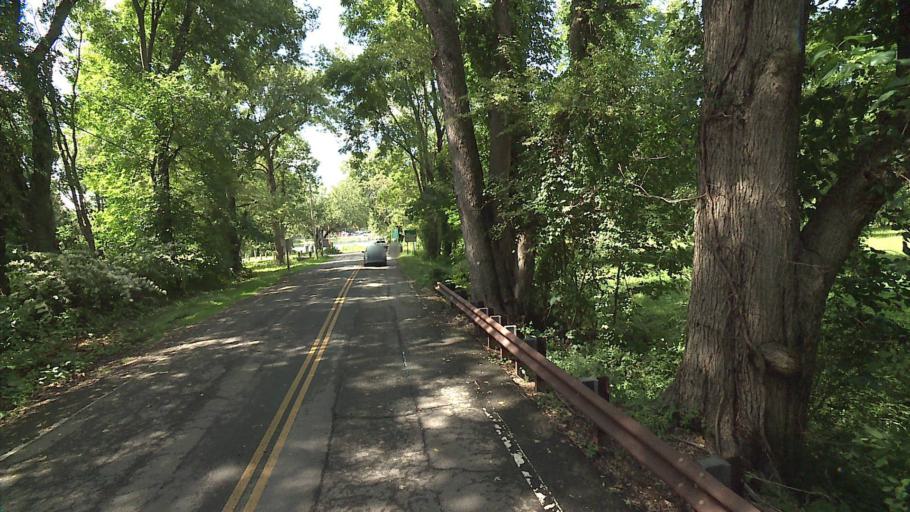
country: US
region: Connecticut
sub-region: Hartford County
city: Glastonbury Center
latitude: 41.6655
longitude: -72.6250
